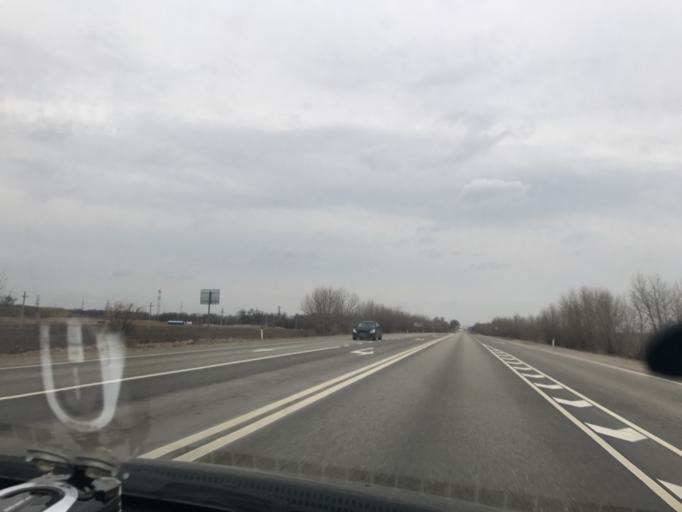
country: RU
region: Krasnodarskiy
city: Parkovyy
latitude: 45.8288
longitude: 40.1860
